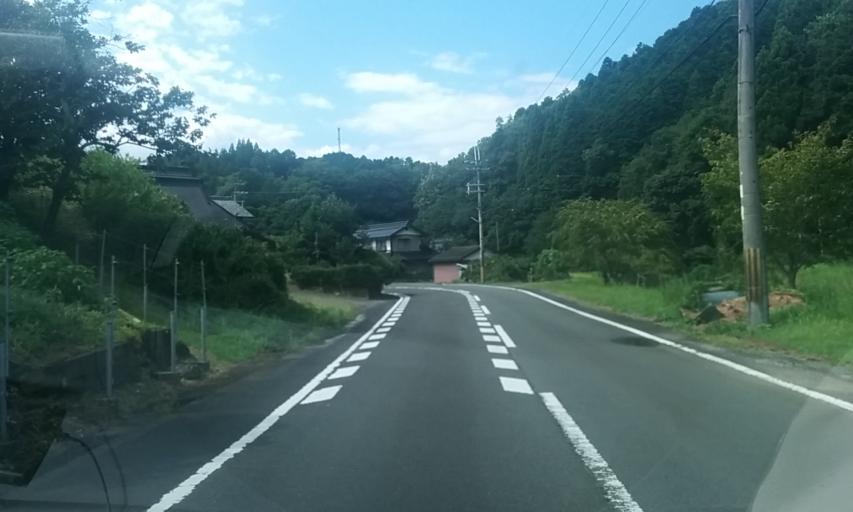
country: JP
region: Kyoto
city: Fukuchiyama
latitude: 35.3703
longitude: 135.1600
